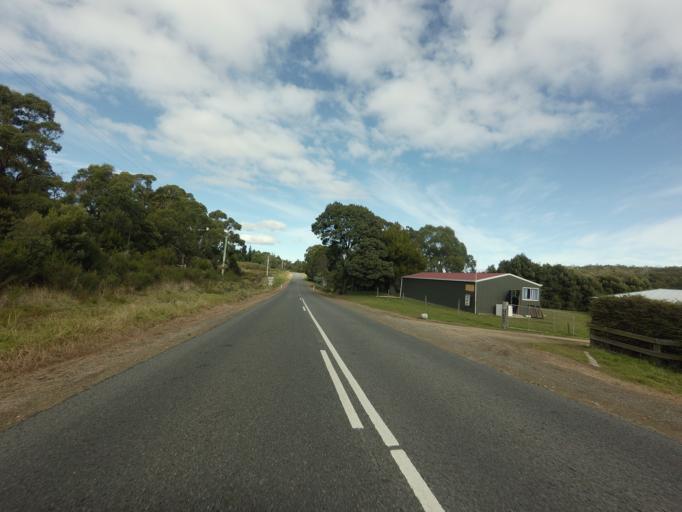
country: AU
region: Tasmania
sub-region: Clarence
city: Sandford
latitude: -43.0843
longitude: 147.7377
